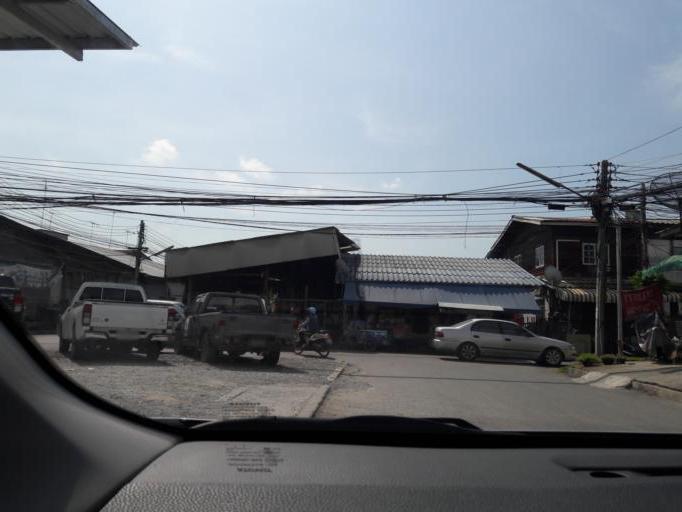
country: TH
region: Ang Thong
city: Ang Thong
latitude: 14.5916
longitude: 100.4493
